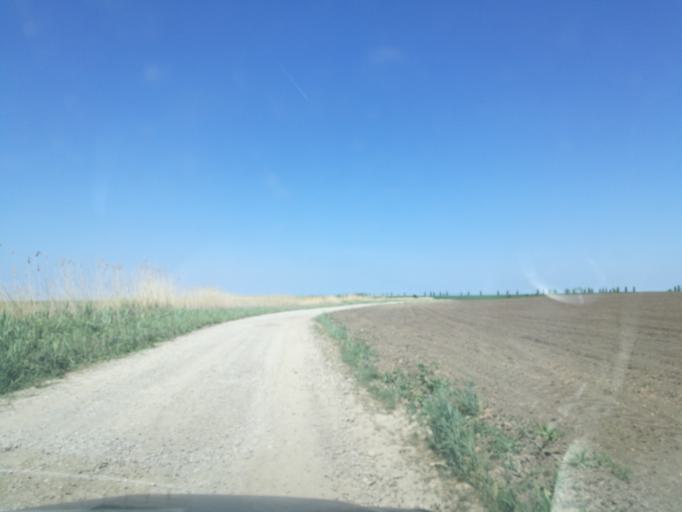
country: RO
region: Ialomita
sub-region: Comuna Adancata
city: Adancata
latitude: 44.7831
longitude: 26.4650
